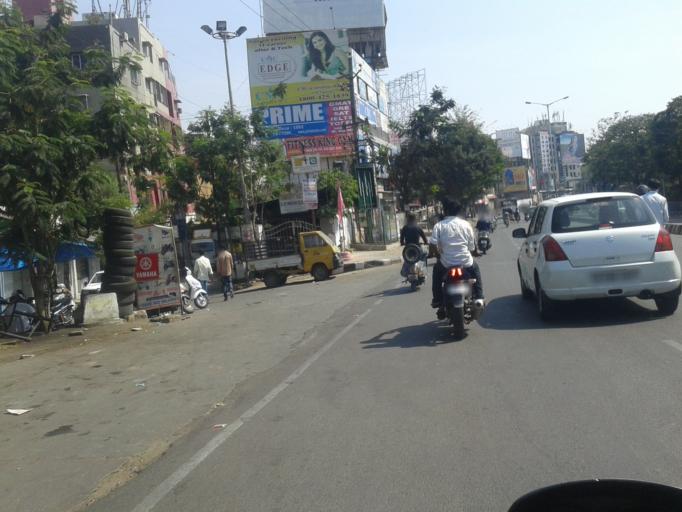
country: IN
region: Telangana
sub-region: Hyderabad
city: Hyderabad
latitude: 17.4084
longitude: 78.4760
